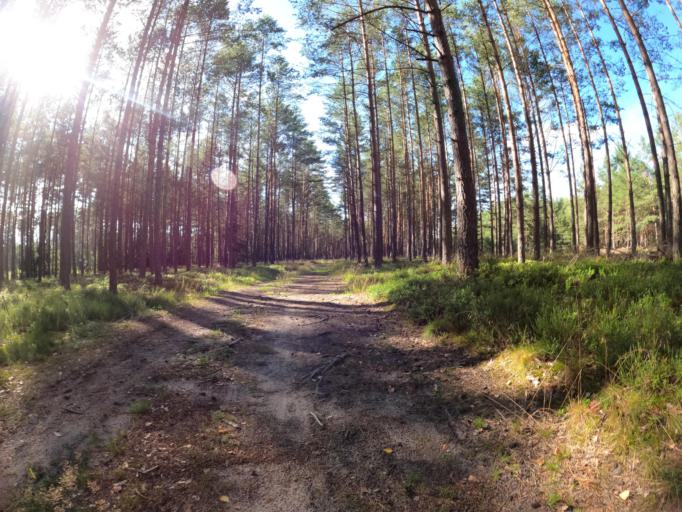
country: PL
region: West Pomeranian Voivodeship
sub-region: Powiat bialogardzki
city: Tychowo
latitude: 54.0488
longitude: 16.3104
